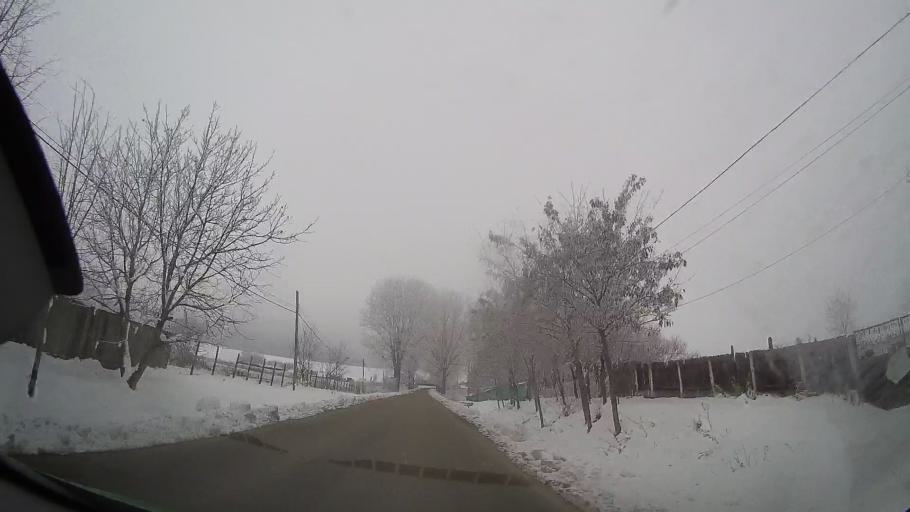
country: RO
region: Neamt
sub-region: Comuna Icusesti
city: Balusesti
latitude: 46.8609
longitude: 27.0126
